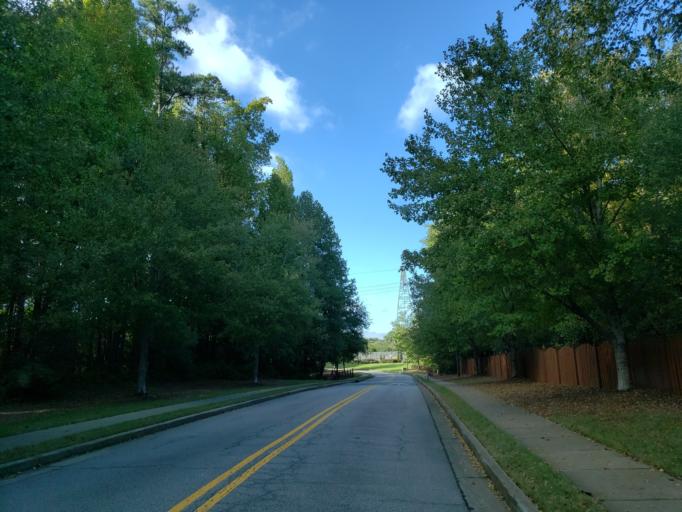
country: US
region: Georgia
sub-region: Cobb County
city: Marietta
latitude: 33.9871
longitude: -84.5035
